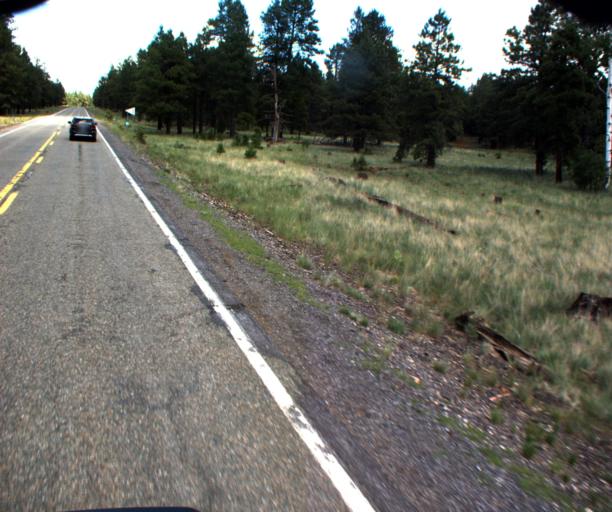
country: US
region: Arizona
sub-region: Coconino County
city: Parks
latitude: 35.3582
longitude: -111.7909
